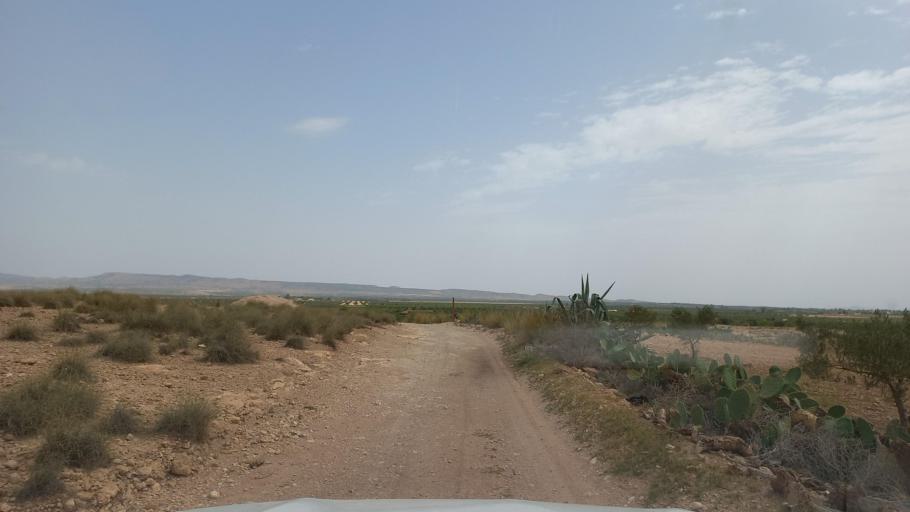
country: TN
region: Al Qasrayn
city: Kasserine
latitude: 35.2919
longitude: 9.0053
